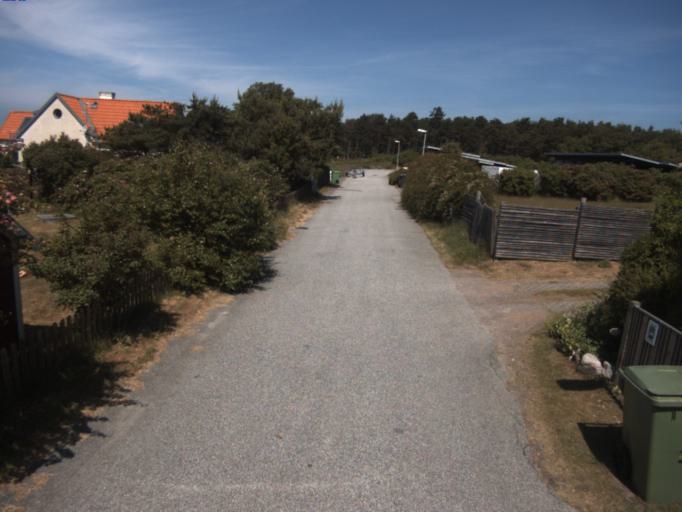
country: DK
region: Capital Region
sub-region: Helsingor Kommune
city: Hellebaek
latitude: 56.1240
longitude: 12.5997
